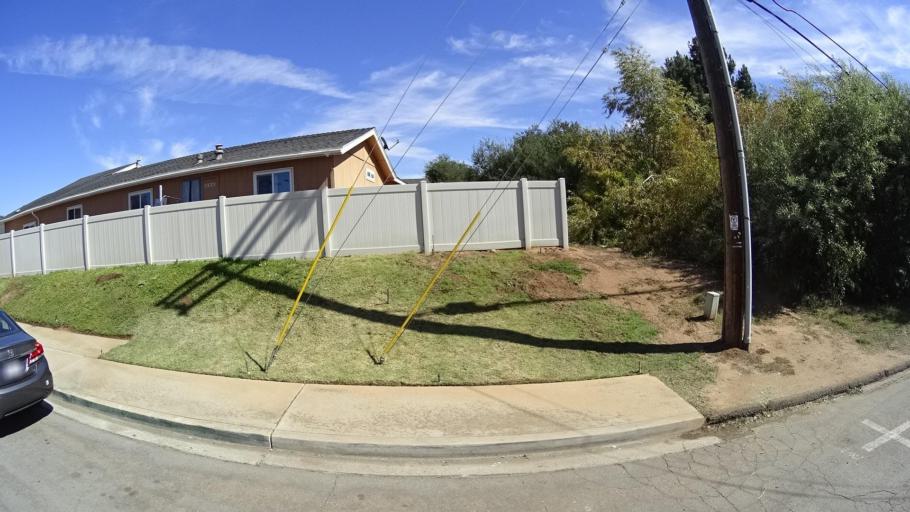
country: US
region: California
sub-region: San Diego County
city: Harbison Canyon
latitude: 32.8592
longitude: -116.8258
